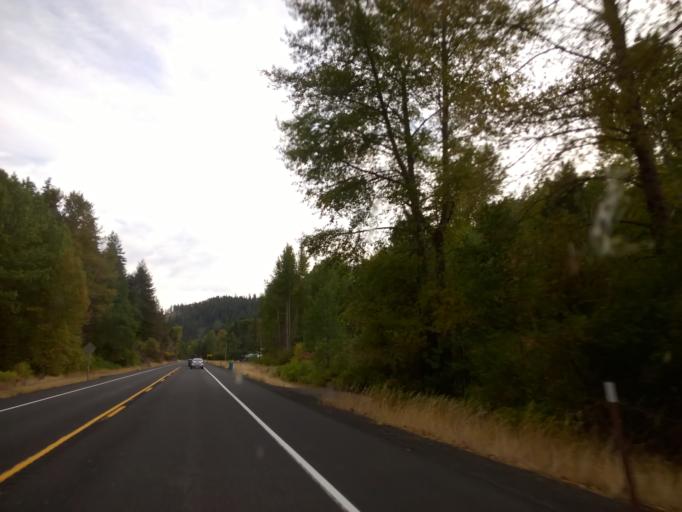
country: US
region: Washington
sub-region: Kittitas County
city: Cle Elum
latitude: 47.2242
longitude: -120.6964
